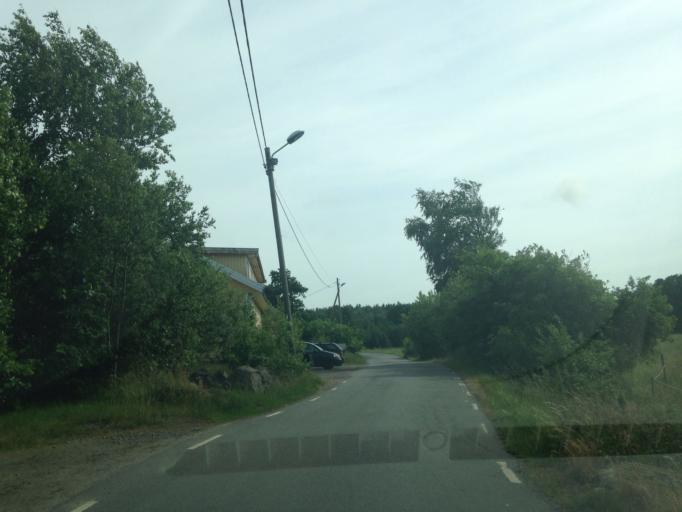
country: SE
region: Vaestra Goetaland
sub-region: Goteborg
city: Majorna
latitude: 57.7550
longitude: 11.8677
